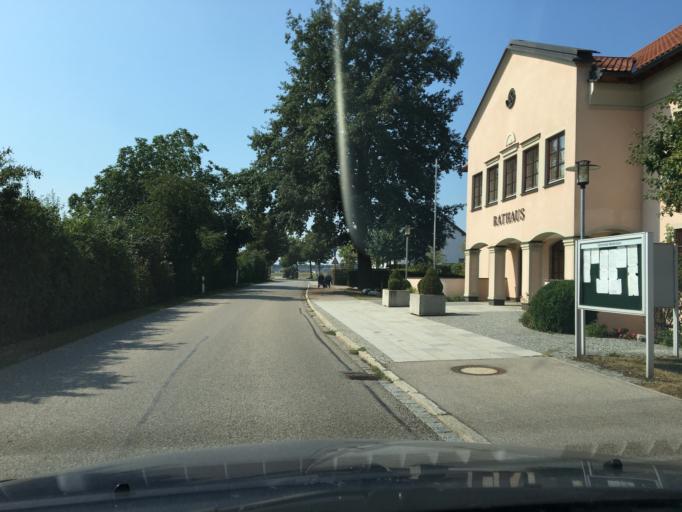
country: DE
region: Bavaria
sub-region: Upper Bavaria
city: Mettenheim
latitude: 48.2639
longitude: 12.4662
